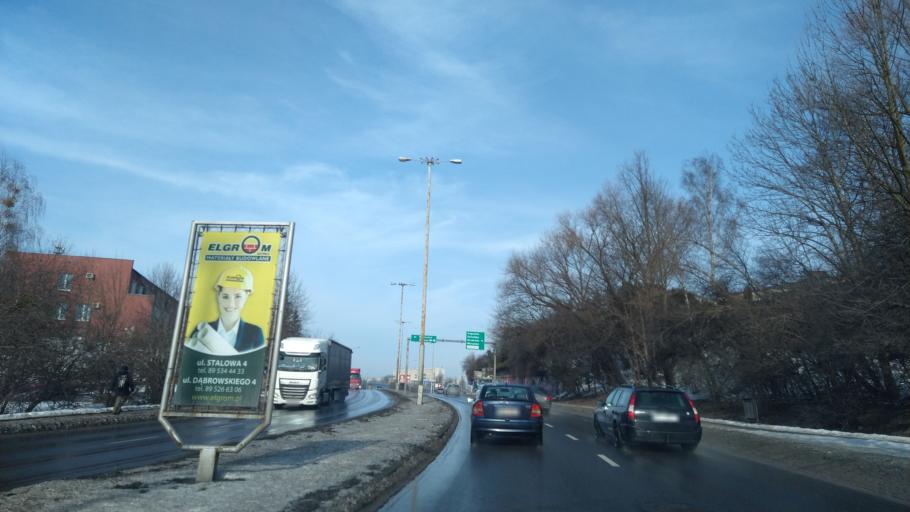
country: PL
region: Warmian-Masurian Voivodeship
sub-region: Powiat olsztynski
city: Olsztyn
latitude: 53.7597
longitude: 20.5001
